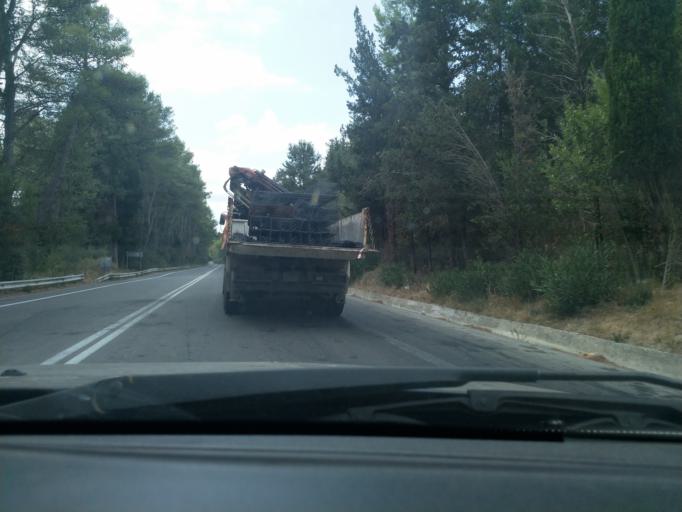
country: GR
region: Crete
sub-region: Nomos Chanias
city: Kalivai
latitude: 35.3916
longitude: 24.1776
